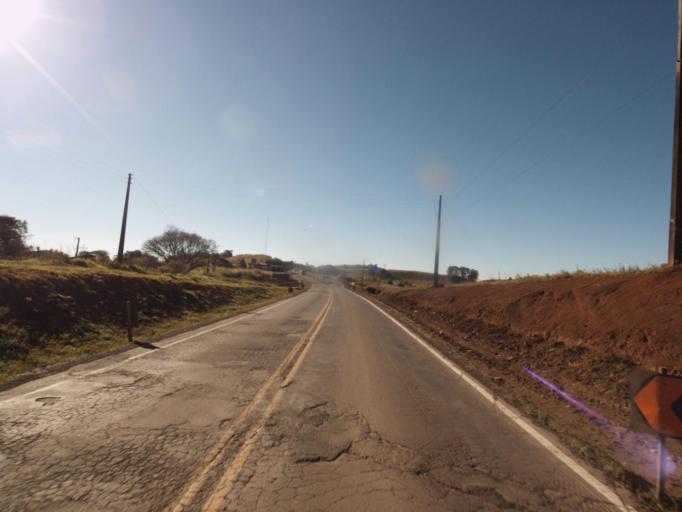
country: AR
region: Misiones
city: Bernardo de Irigoyen
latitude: -26.6408
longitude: -53.5183
